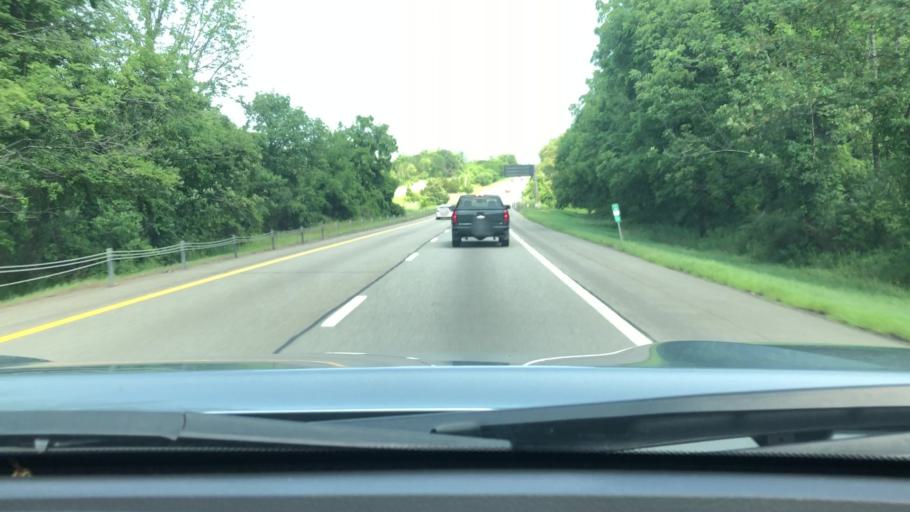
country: US
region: New York
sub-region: Dutchess County
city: Brinckerhoff
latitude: 41.5313
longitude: -73.8418
